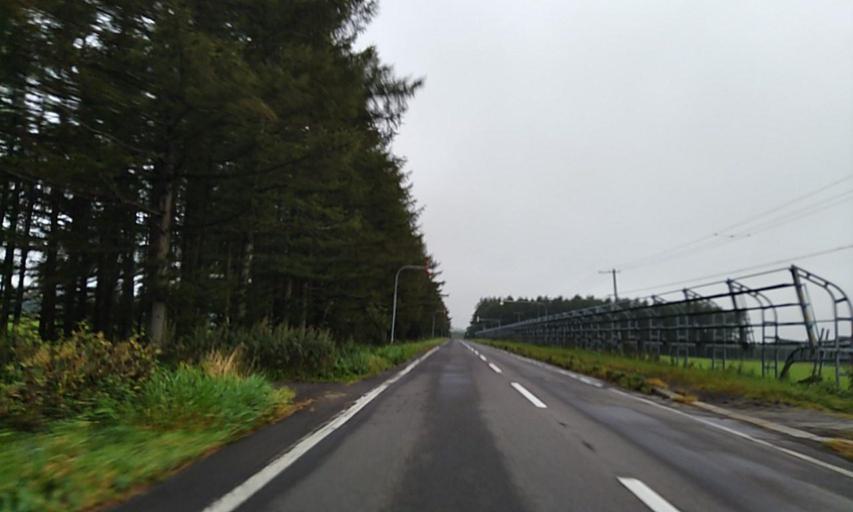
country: JP
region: Hokkaido
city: Shibetsu
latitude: 43.4929
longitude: 144.6436
